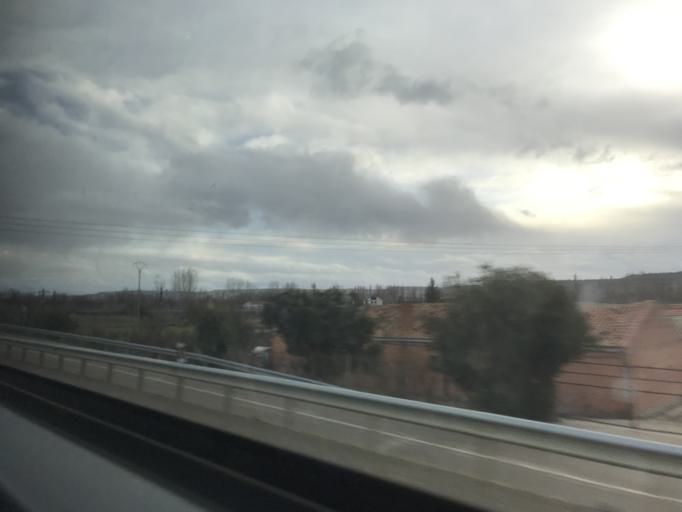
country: ES
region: Castille and Leon
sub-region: Provincia de Palencia
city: Grijota
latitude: 42.0324
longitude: -4.5559
